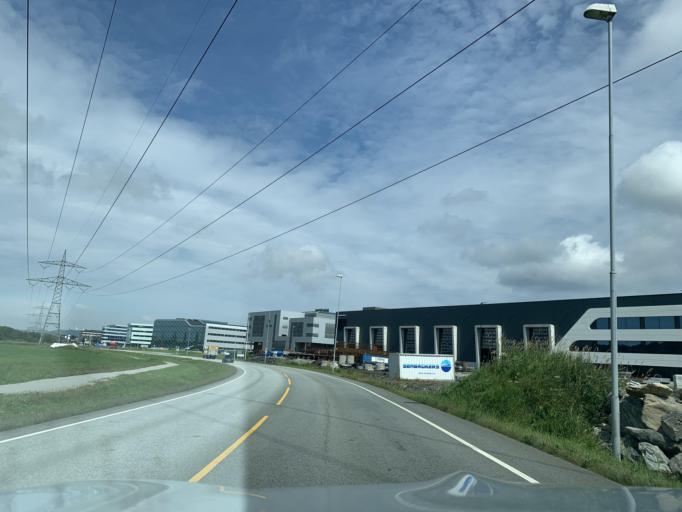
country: NO
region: Rogaland
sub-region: Sola
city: Sola
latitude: 58.8847
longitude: 5.6950
